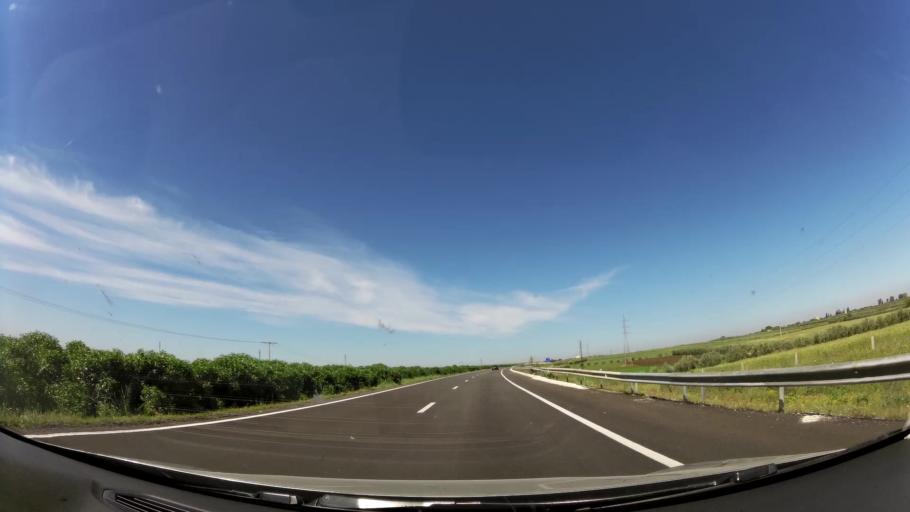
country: MA
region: Meknes-Tafilalet
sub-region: Meknes
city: Meknes
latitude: 33.8295
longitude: -5.4916
